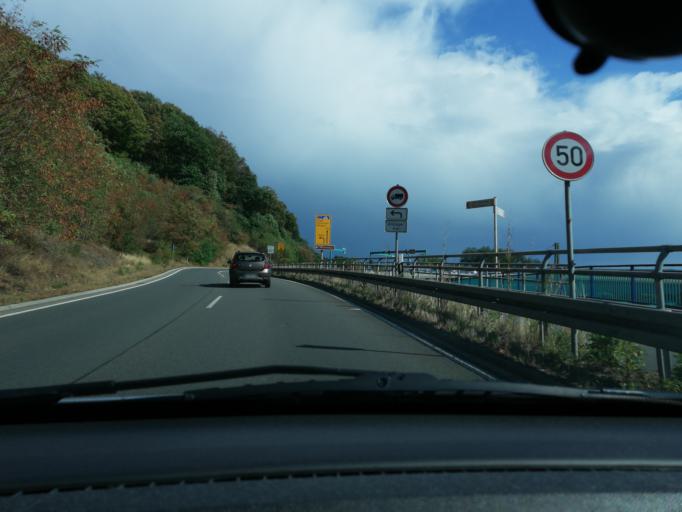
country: DE
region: North Rhine-Westphalia
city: Wetter (Ruhr)
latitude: 51.3918
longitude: 7.3779
